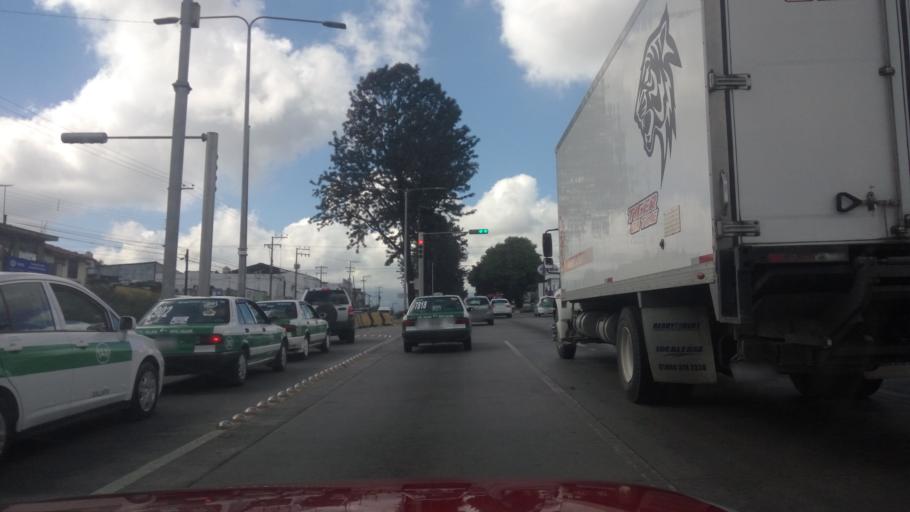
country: MX
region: Veracruz
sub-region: Xalapa
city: Xalapa de Enriquez
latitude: 19.5588
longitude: -96.9190
